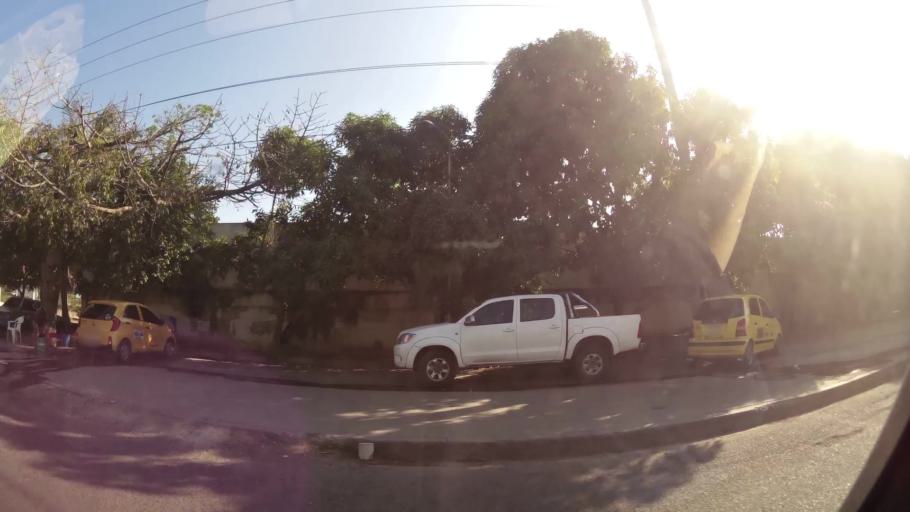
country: CO
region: Bolivar
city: Cartagena
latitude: 10.4061
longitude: -75.4945
